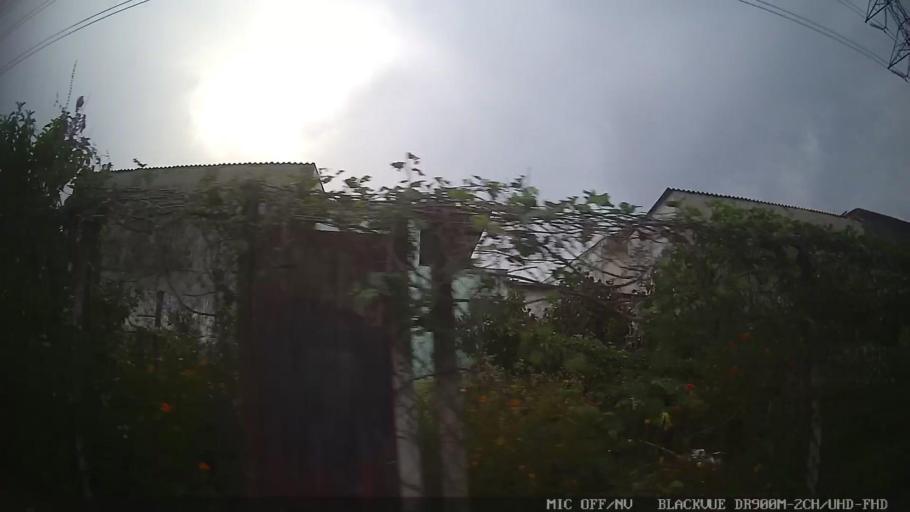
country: BR
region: Sao Paulo
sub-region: Suzano
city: Suzano
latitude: -23.5398
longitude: -46.2991
